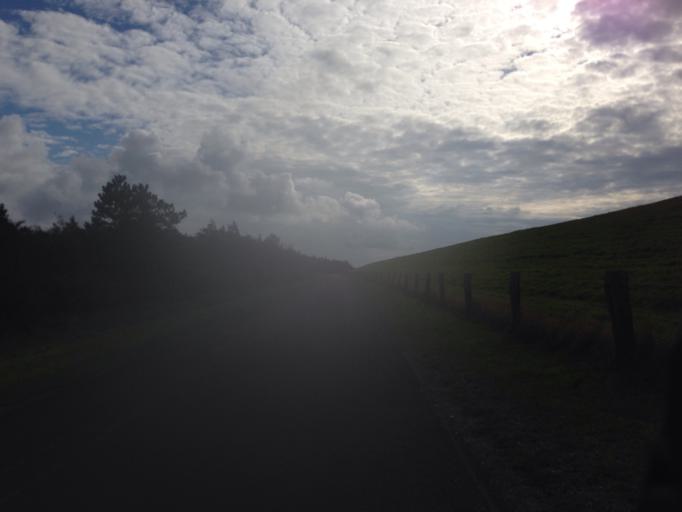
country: DE
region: Schleswig-Holstein
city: Utersum
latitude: 54.7256
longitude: 8.4029
